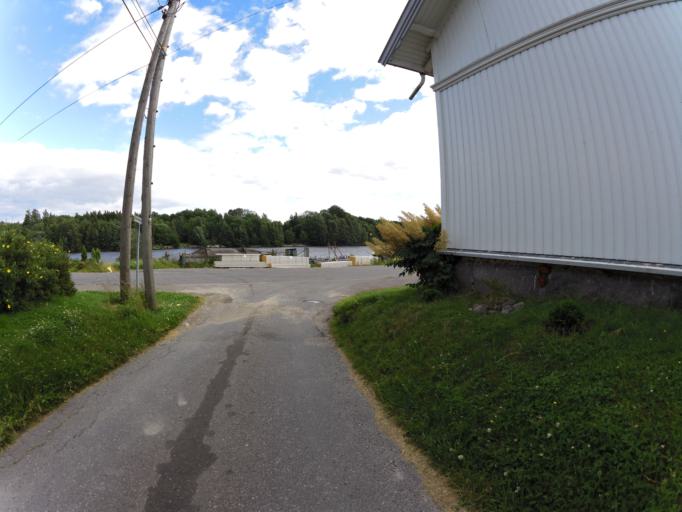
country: NO
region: Ostfold
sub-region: Fredrikstad
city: Fredrikstad
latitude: 59.2424
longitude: 11.0016
